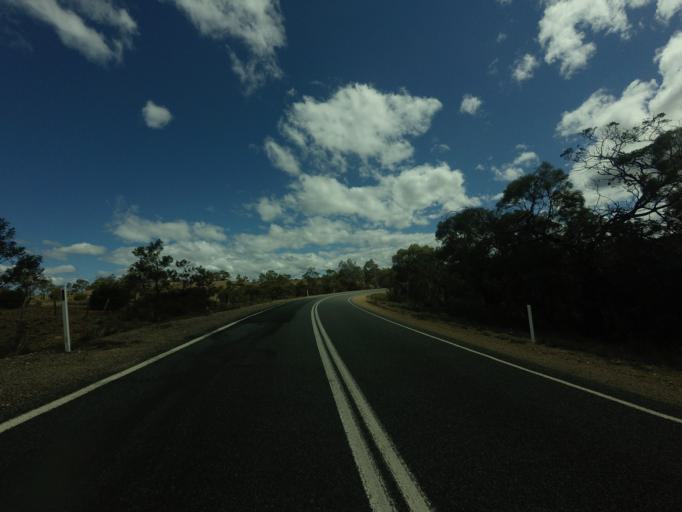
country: AU
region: Tasmania
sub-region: Break O'Day
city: St Helens
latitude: -42.0165
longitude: 147.9872
